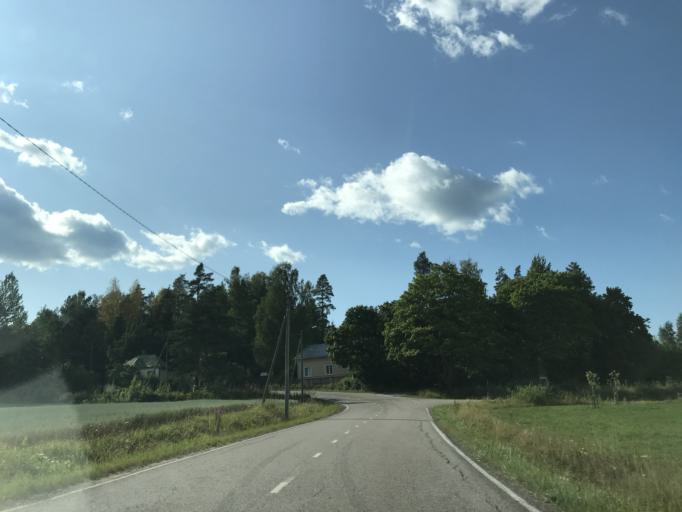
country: FI
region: Uusimaa
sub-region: Helsinki
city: Nurmijaervi
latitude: 60.4541
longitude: 24.6047
